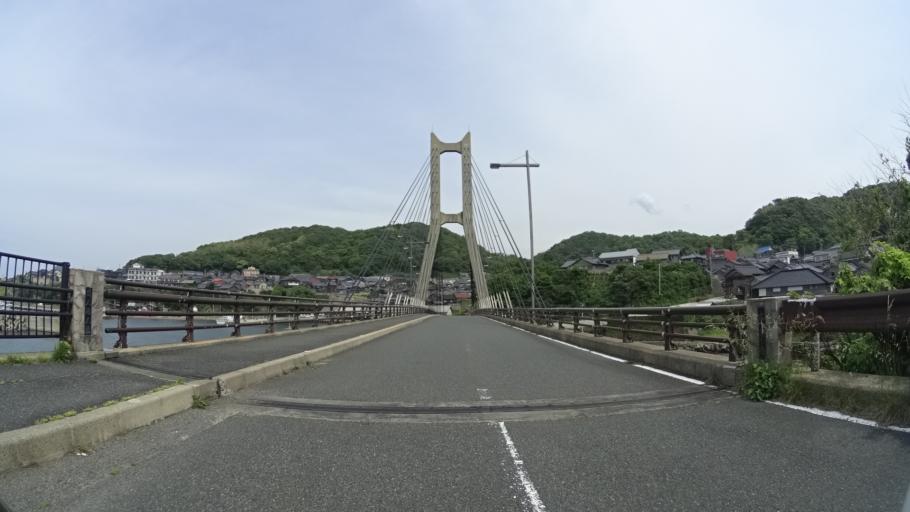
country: JP
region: Kyoto
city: Miyazu
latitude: 35.7391
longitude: 135.0907
